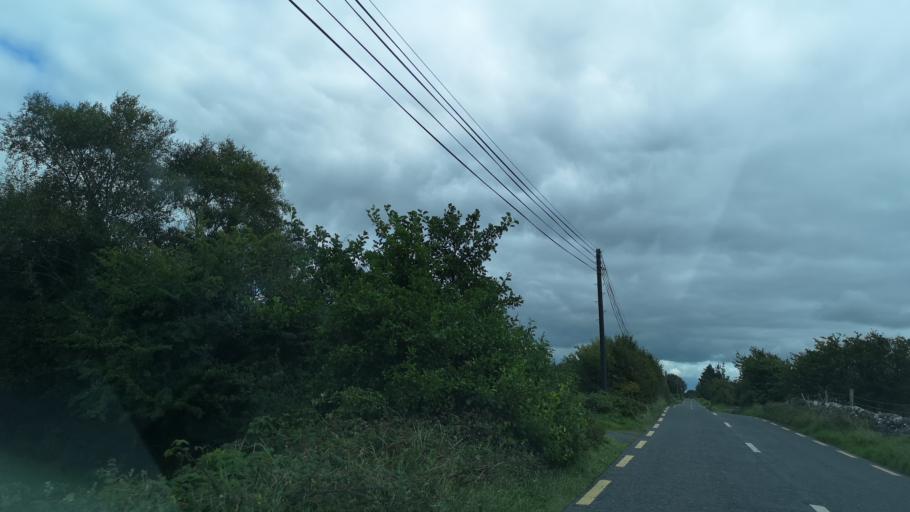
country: IE
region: Connaught
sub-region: County Galway
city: Ballinasloe
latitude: 53.3110
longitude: -8.1585
